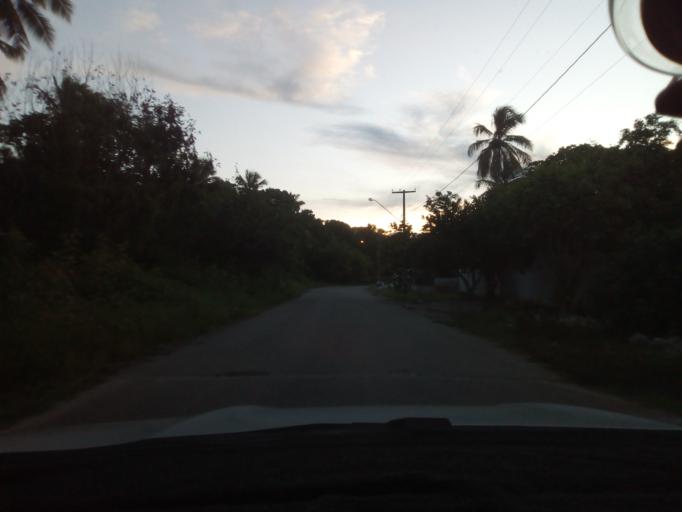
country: BR
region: Paraiba
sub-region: Joao Pessoa
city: Joao Pessoa
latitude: -7.2009
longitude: -34.8031
